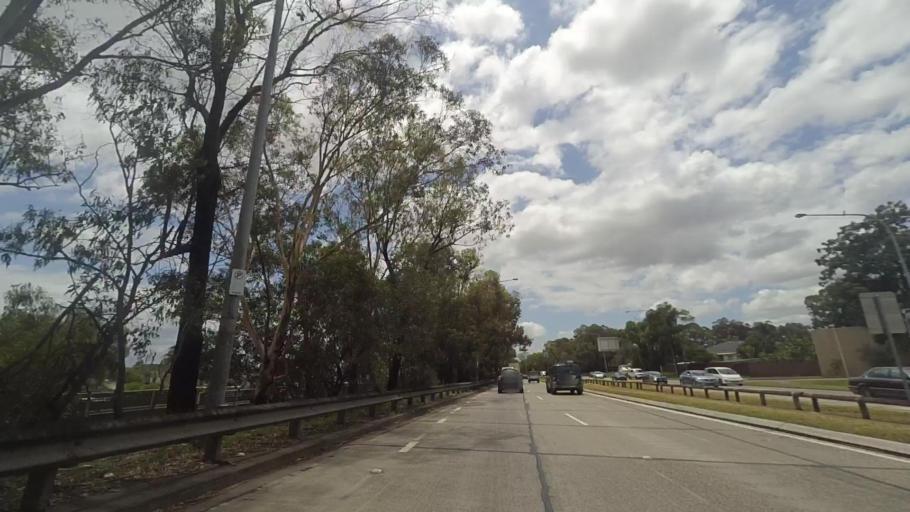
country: AU
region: New South Wales
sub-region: Fairfield
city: Cabramatta West
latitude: -33.8981
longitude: 150.9200
